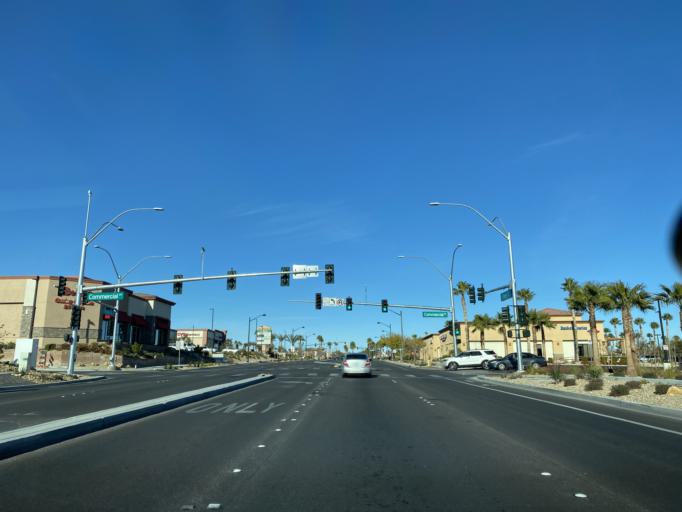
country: US
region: Nevada
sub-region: Clark County
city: Summerlin South
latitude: 36.2996
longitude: -115.2806
